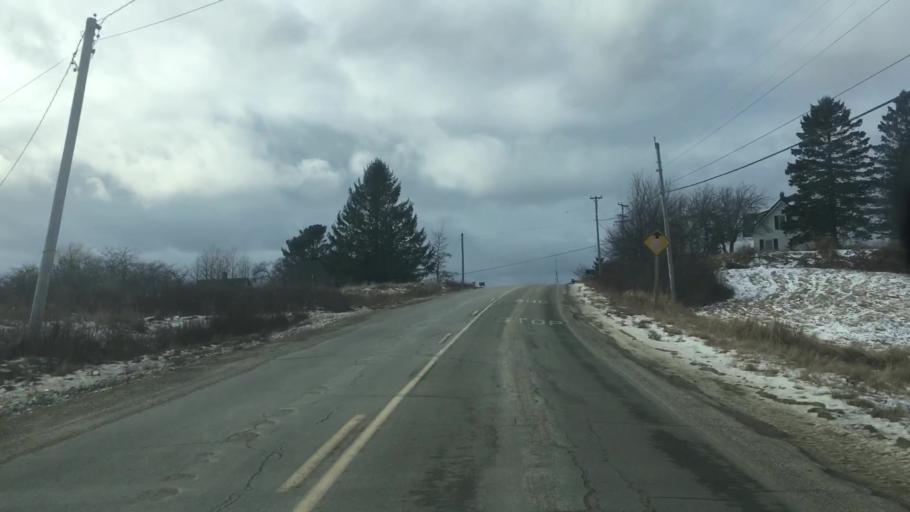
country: US
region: Maine
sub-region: Washington County
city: Machias
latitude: 44.6633
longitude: -67.5534
